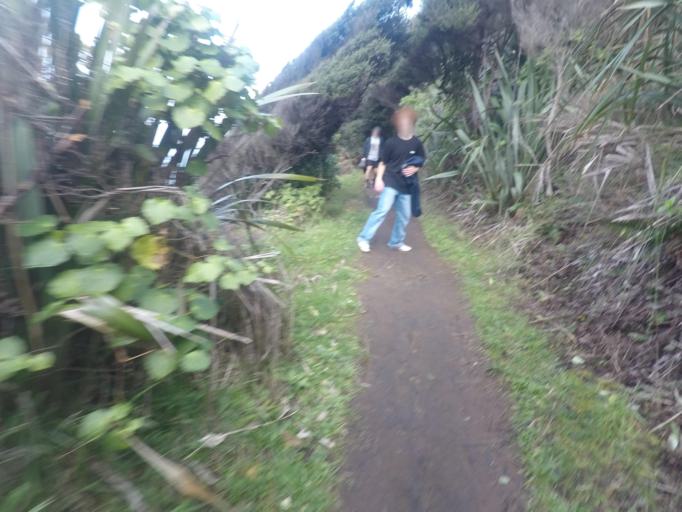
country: NZ
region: Auckland
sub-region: Auckland
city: Muriwai Beach
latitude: -36.8894
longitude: 174.4457
